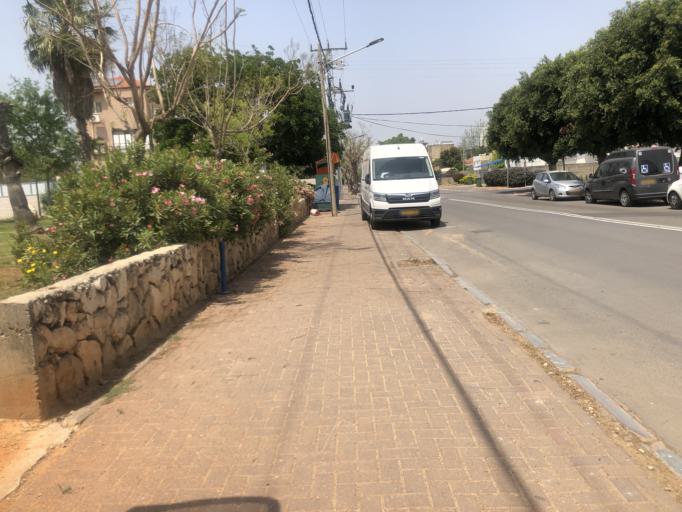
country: IL
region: Central District
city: Rosh Ha'Ayin
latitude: 32.1008
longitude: 34.9410
